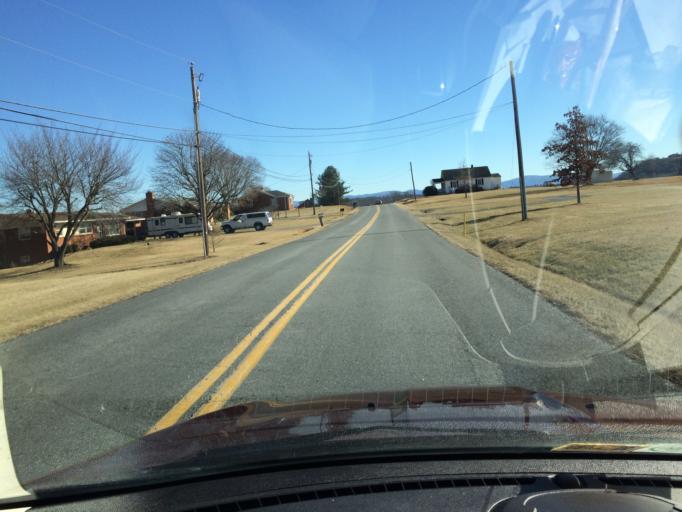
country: US
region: Virginia
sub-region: Rockingham County
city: Bridgewater
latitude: 38.3656
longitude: -78.9677
